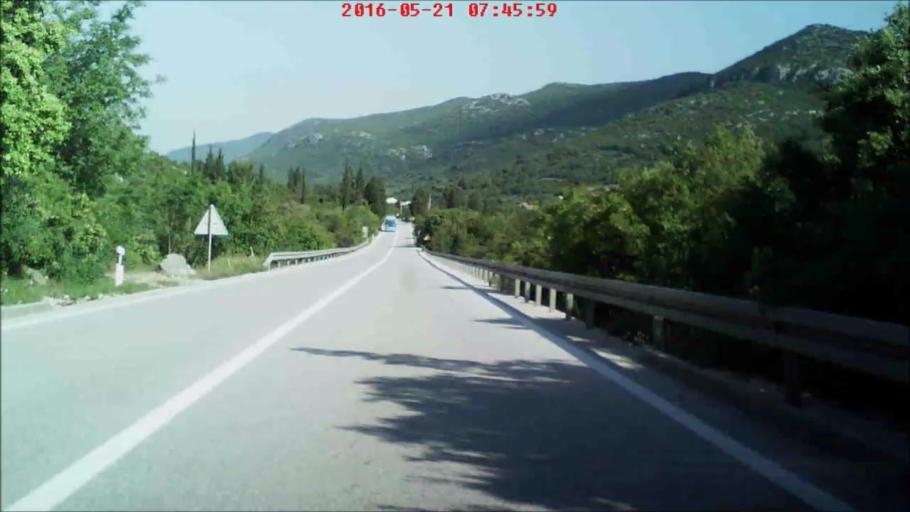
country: HR
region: Dubrovacko-Neretvanska
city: Ston
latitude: 42.8253
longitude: 17.7573
